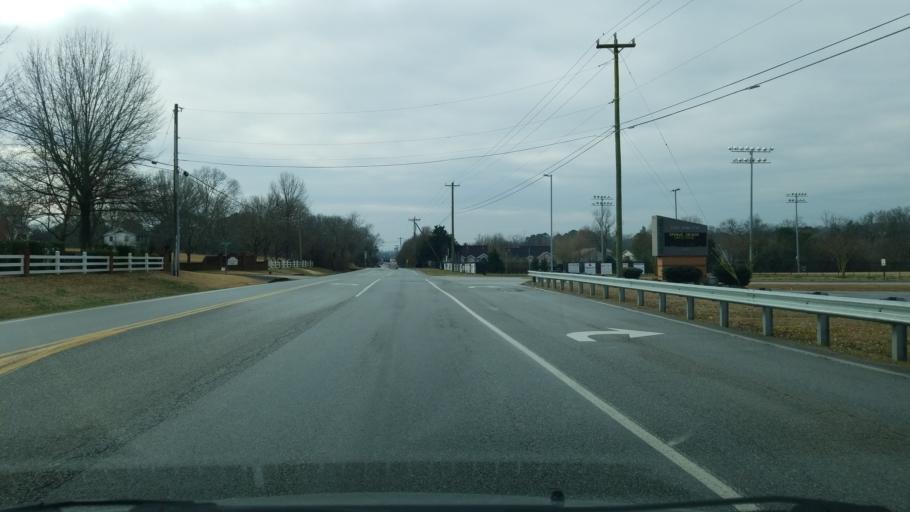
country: US
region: Tennessee
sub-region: Hamilton County
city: East Brainerd
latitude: 35.0047
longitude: -85.0922
